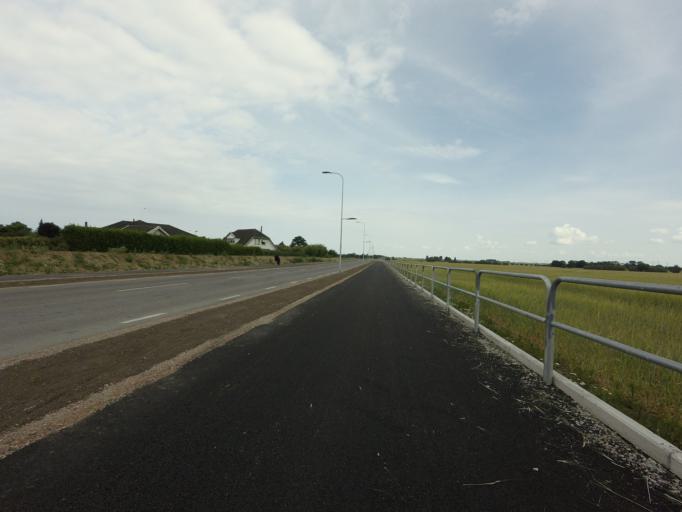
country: SE
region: Skane
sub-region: Staffanstorps Kommun
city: Hjaerup
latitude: 55.6532
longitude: 13.1248
